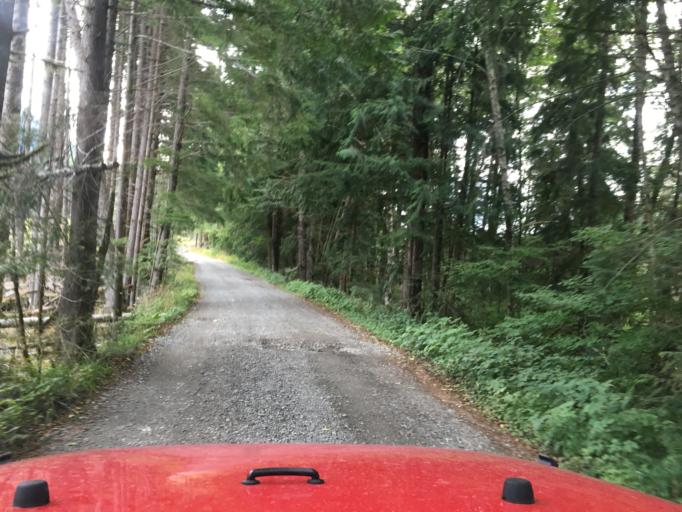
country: US
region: Washington
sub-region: Snohomish County
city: Gold Bar
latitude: 47.6570
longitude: -121.6341
